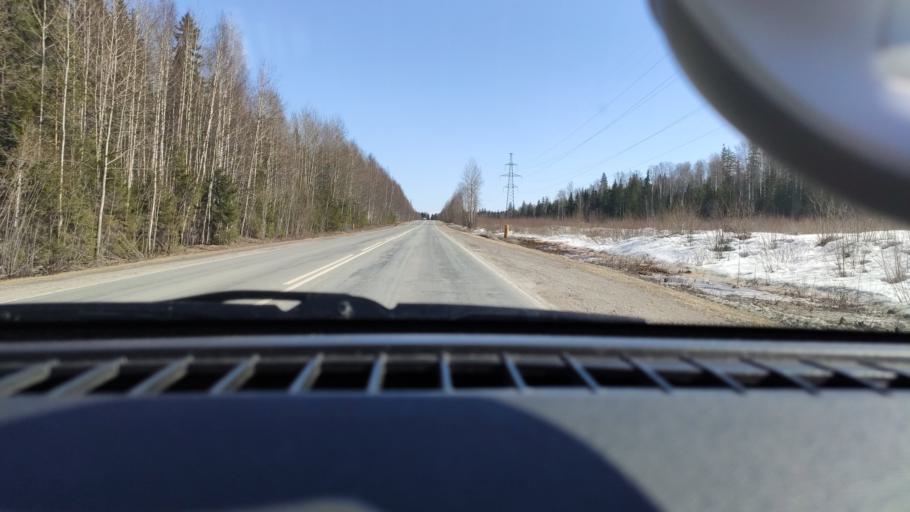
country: RU
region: Perm
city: Perm
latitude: 58.1374
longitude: 56.2819
